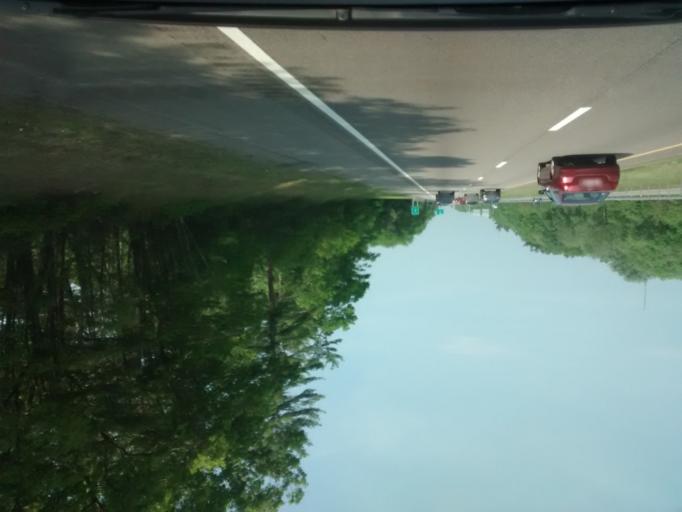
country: US
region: Massachusetts
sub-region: Plymouth County
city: Middleborough Center
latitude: 41.8945
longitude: -70.9508
